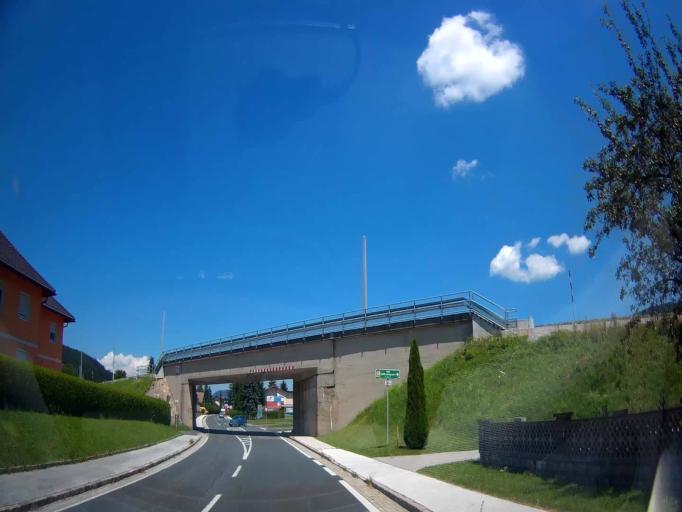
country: AT
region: Carinthia
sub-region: Politischer Bezirk Volkermarkt
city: Bleiburg/Pliberk
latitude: 46.5824
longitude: 14.7960
